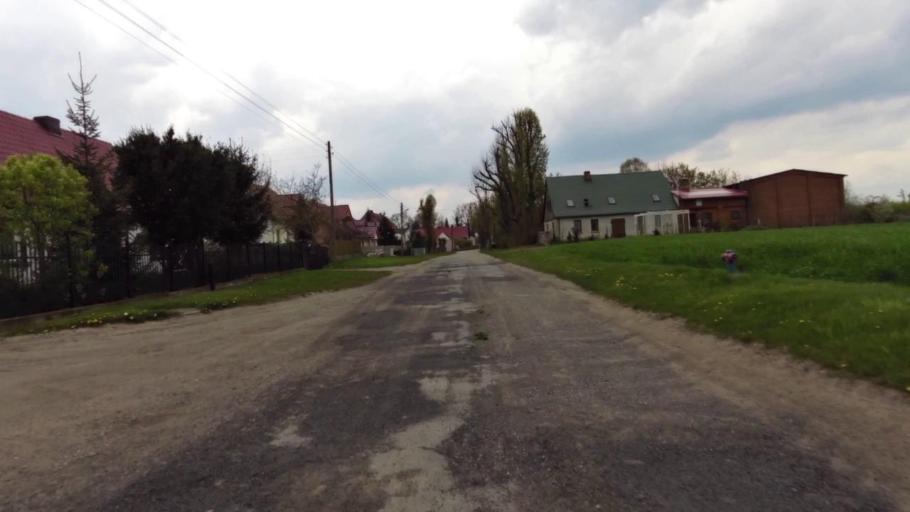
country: PL
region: West Pomeranian Voivodeship
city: Trzcinsko Zdroj
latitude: 52.9644
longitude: 14.6733
